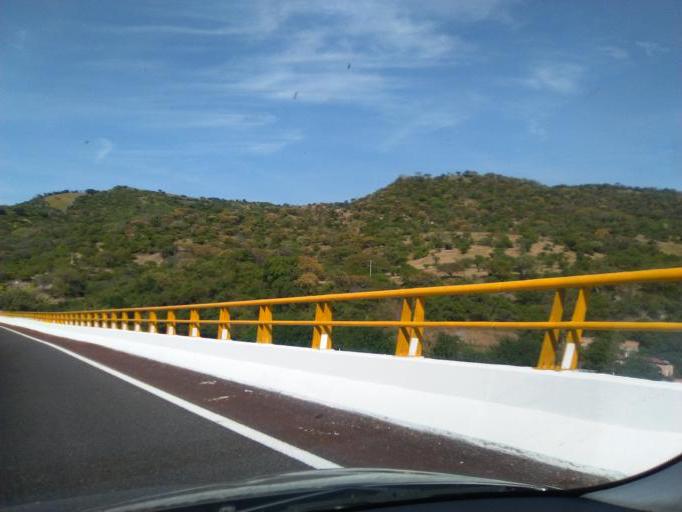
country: MX
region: Guerrero
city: Copalillo
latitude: 18.1092
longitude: -99.2050
